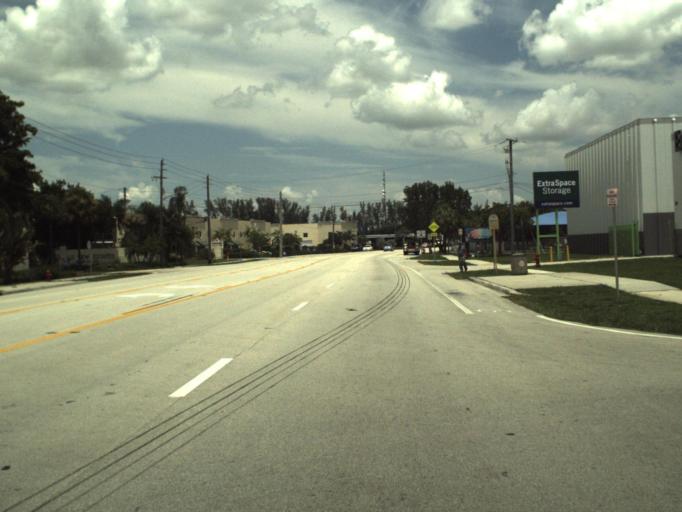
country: US
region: Florida
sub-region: Broward County
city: Coconut Creek
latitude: 26.2388
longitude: -80.1656
